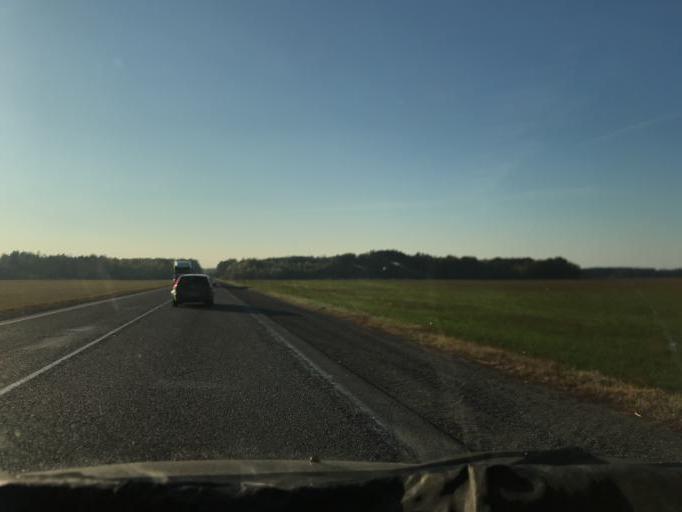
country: BY
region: Gomel
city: Zhytkavichy
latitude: 52.2727
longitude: 28.0259
